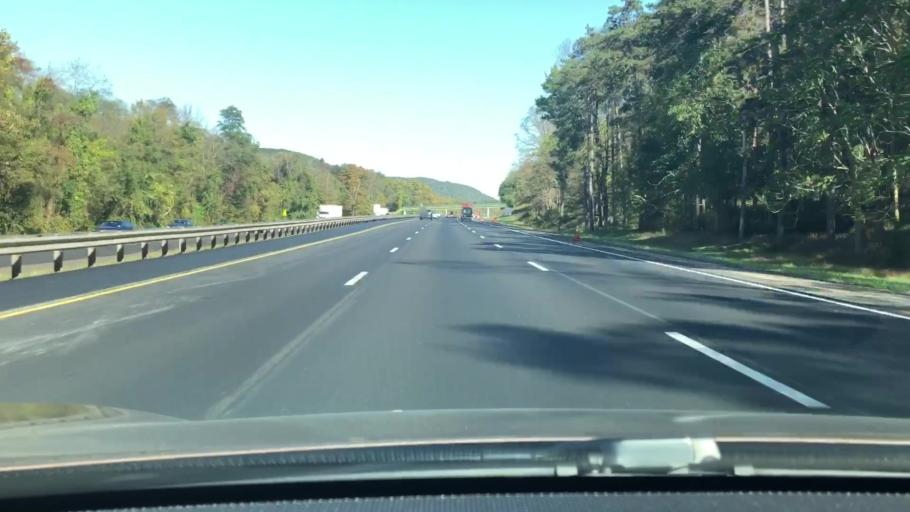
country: US
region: New York
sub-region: Orange County
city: Harriman
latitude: 41.2408
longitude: -74.1716
